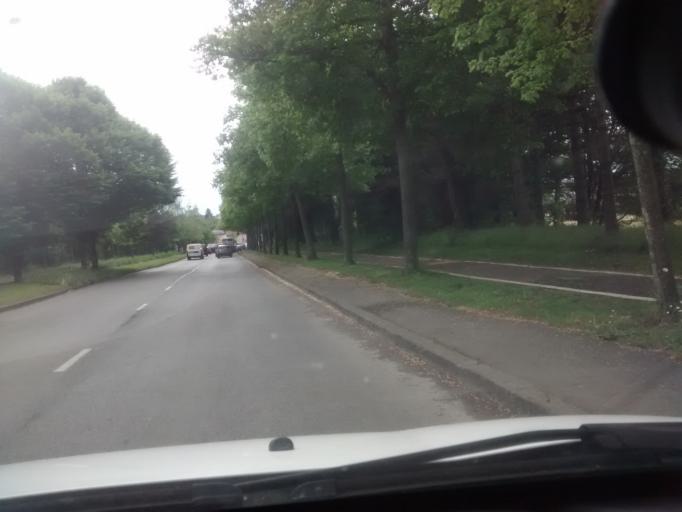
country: FR
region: Brittany
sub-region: Departement d'Ille-et-Vilaine
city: Rennes
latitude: 48.1291
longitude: -1.6804
